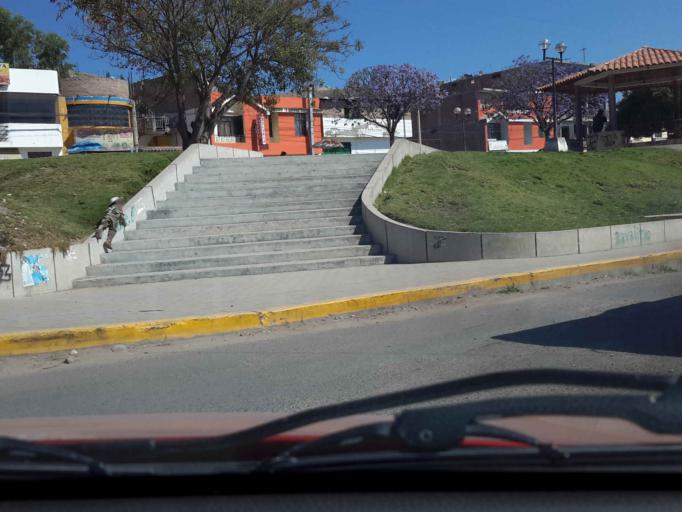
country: PE
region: Ayacucho
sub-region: Provincia de Huamanga
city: Ayacucho
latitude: -13.1436
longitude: -74.2282
